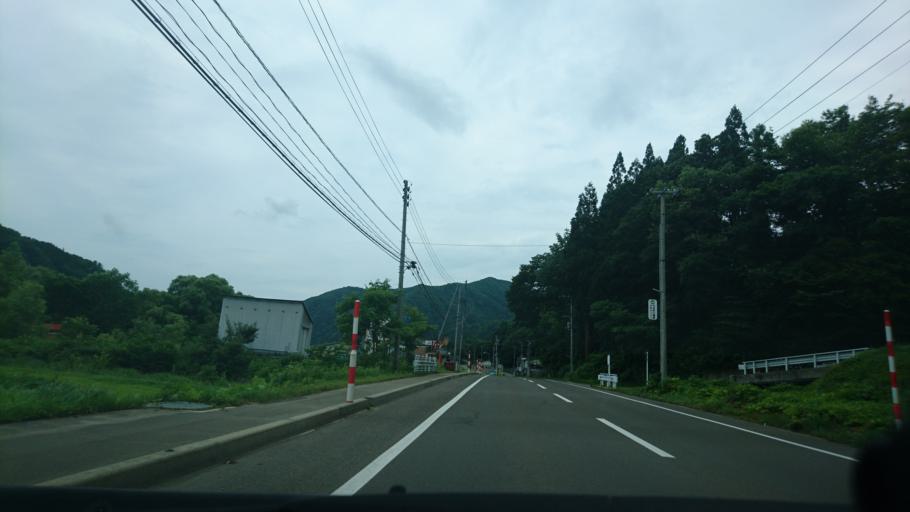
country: JP
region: Akita
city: Yuzawa
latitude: 39.1743
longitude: 140.7101
